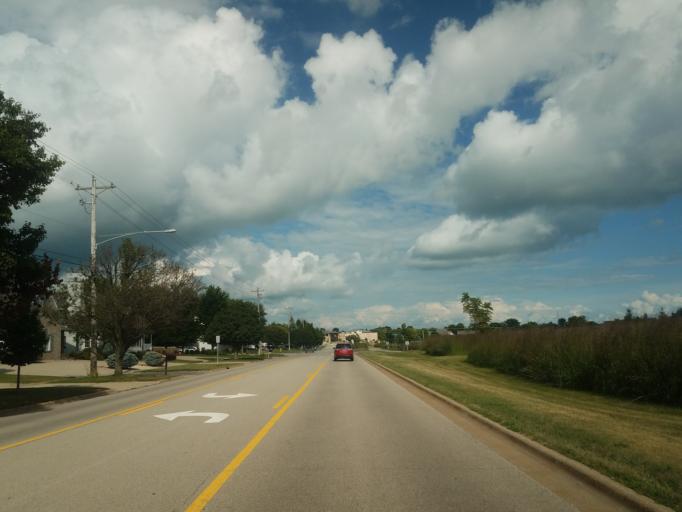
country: US
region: Illinois
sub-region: McLean County
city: Normal
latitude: 40.5104
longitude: -88.9290
